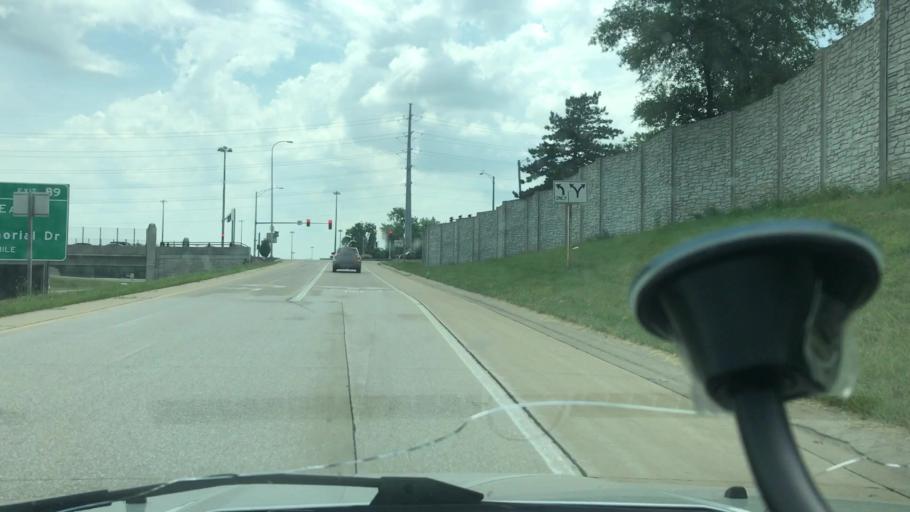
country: US
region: Illinois
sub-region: Peoria County
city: West Peoria
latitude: 40.7376
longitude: -89.6330
